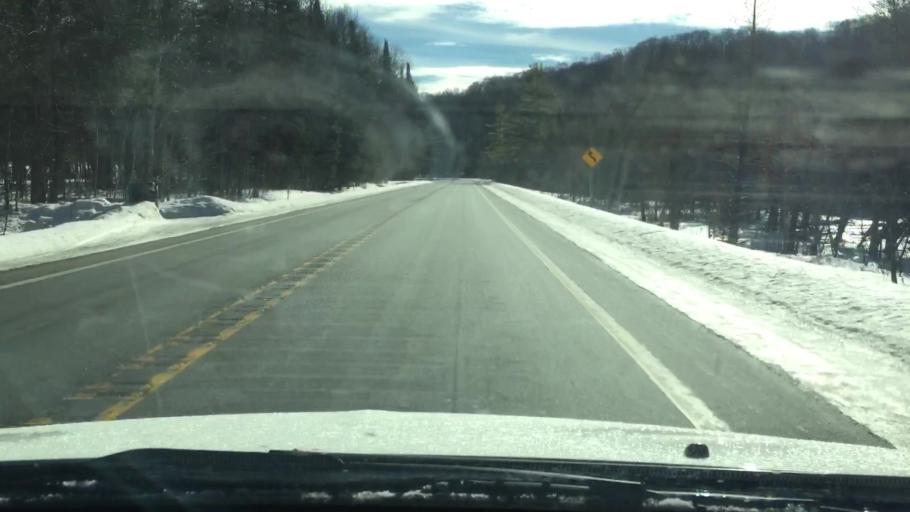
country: US
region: Michigan
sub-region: Antrim County
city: Mancelona
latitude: 45.0036
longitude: -85.0629
